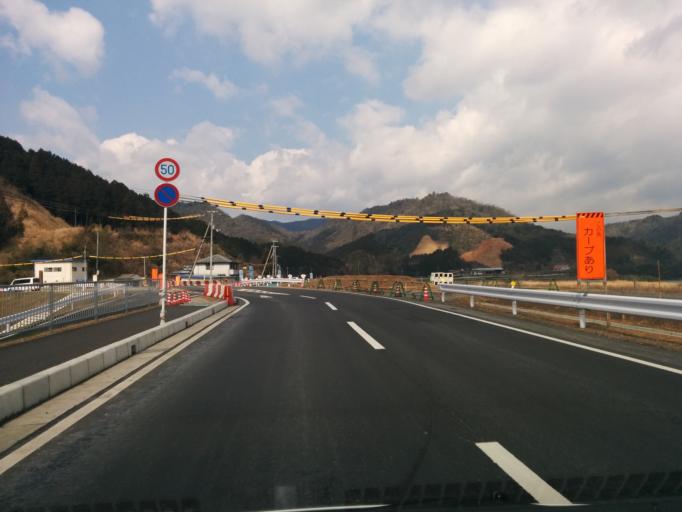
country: JP
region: Kyoto
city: Fukuchiyama
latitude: 35.4005
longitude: 135.1827
